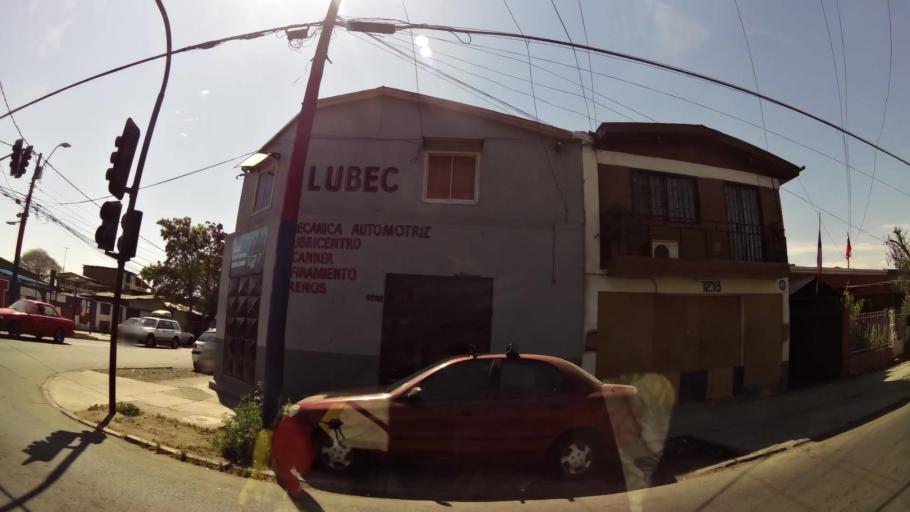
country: CL
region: Santiago Metropolitan
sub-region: Provincia de Santiago
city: La Pintana
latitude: -33.5319
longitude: -70.6488
